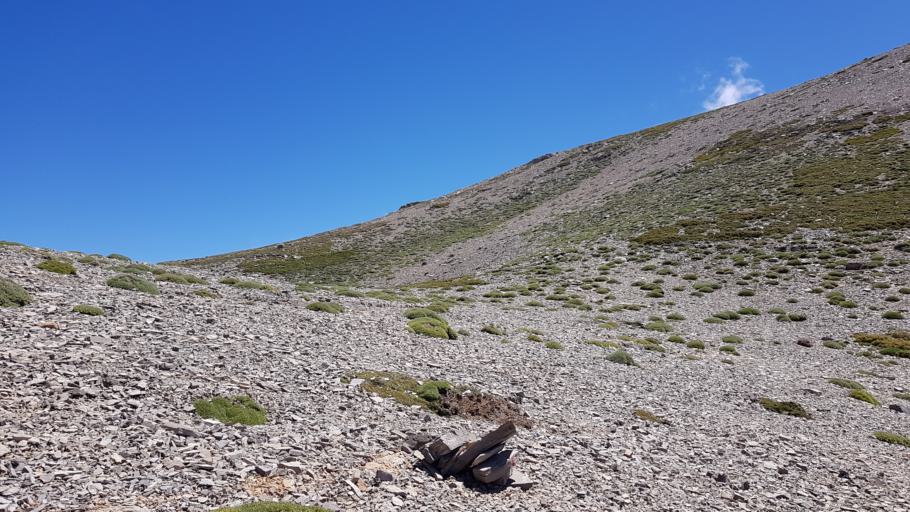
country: GR
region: Crete
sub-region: Nomos Rethymnis
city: Zoniana
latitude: 35.2211
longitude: 24.7792
